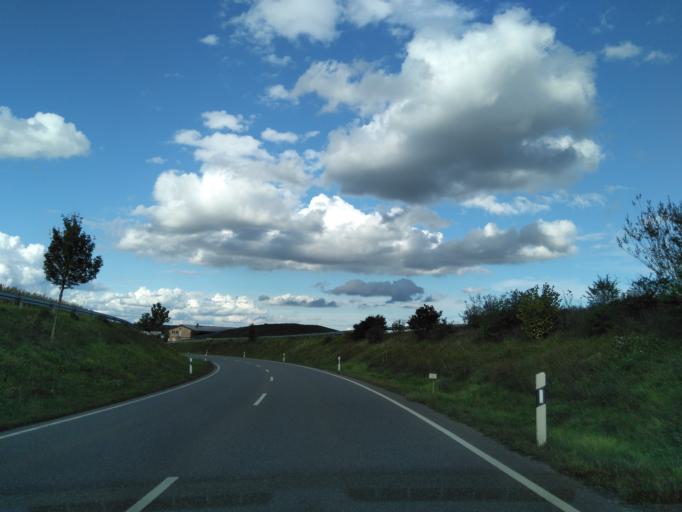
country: DE
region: Baden-Wuerttemberg
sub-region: Regierungsbezirk Stuttgart
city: Bietigheim-Bissingen
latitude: 48.9522
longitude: 9.0756
